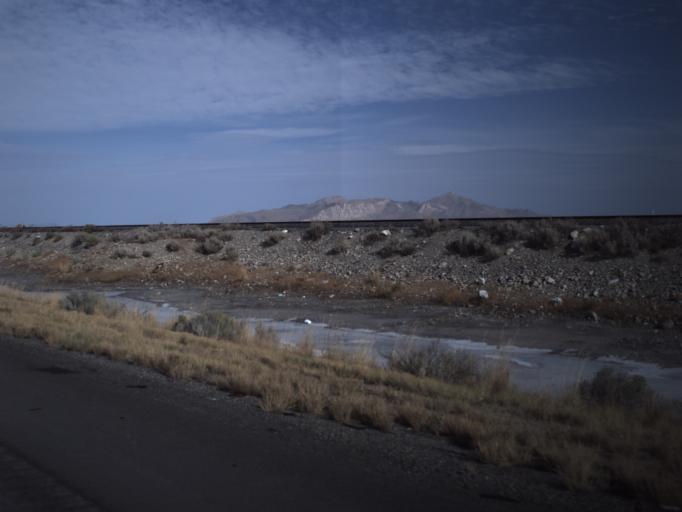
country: US
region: Utah
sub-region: Tooele County
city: Grantsville
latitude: 40.6736
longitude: -112.3940
